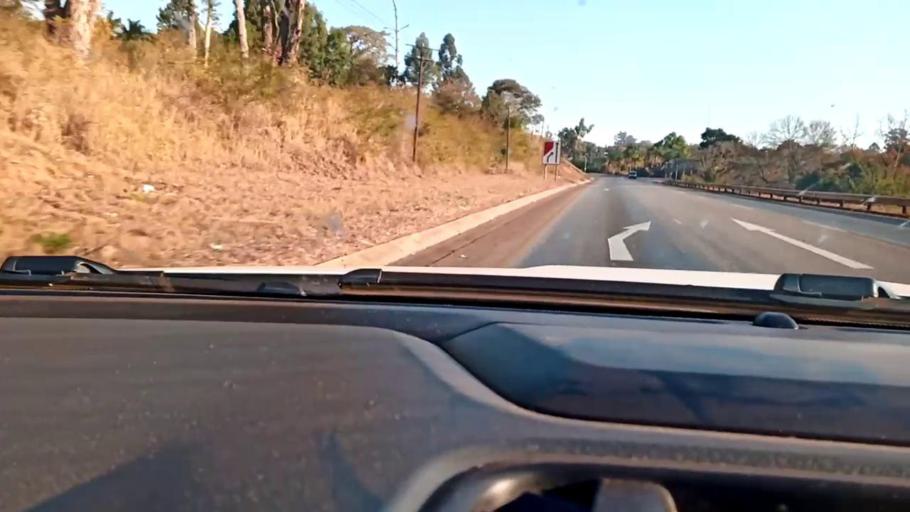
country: ZA
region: Limpopo
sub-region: Mopani District Municipality
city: Duiwelskloof
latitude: -23.6880
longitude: 30.1475
